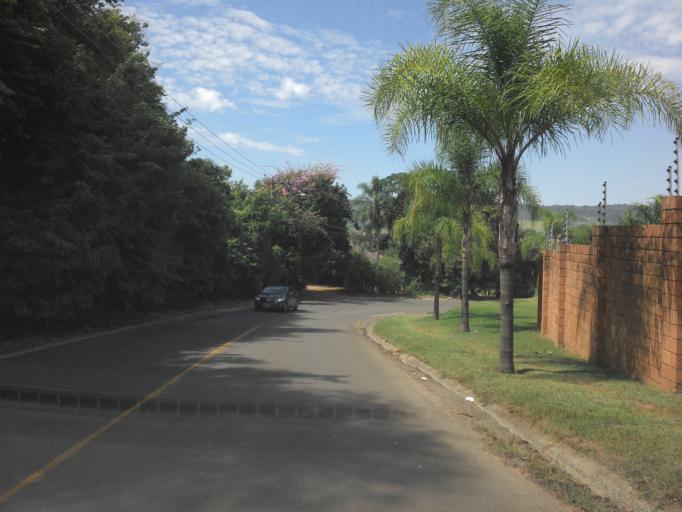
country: BR
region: Sao Paulo
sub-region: Valinhos
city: Valinhos
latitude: -22.9404
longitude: -46.9837
